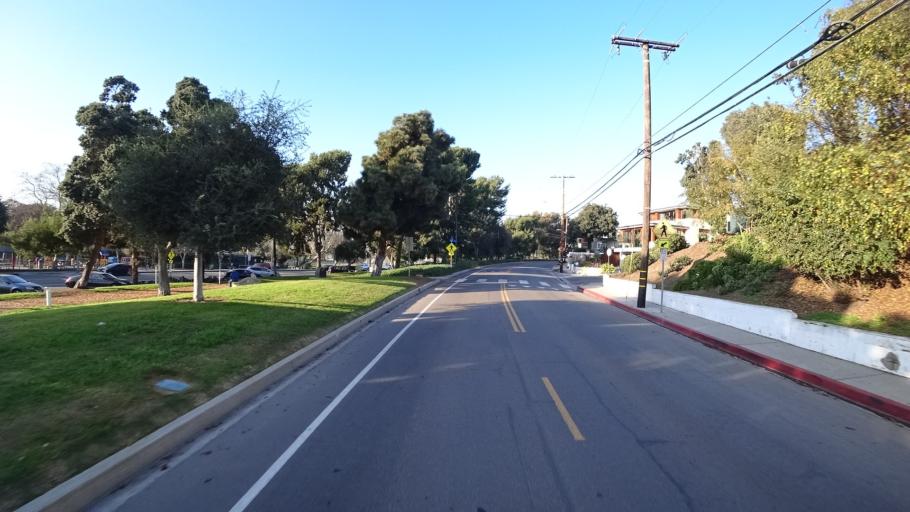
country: US
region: California
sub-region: Los Angeles County
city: Manhattan Beach
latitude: 33.8899
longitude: -118.4096
